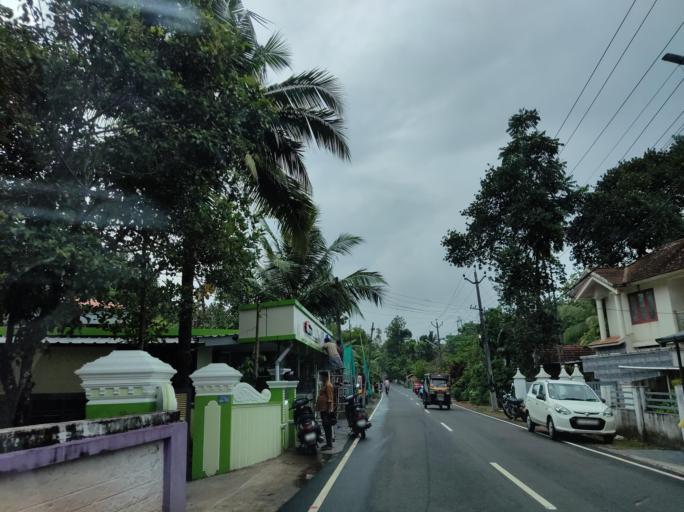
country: IN
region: Kerala
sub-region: Alappuzha
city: Mavelikara
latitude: 9.2418
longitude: 76.5529
